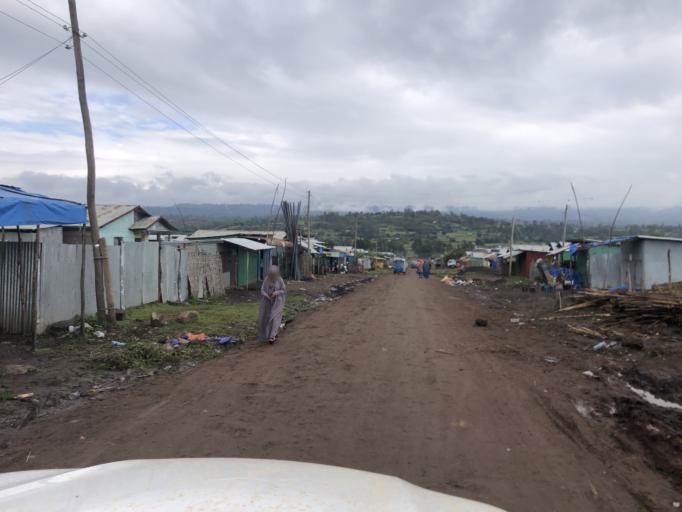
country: ET
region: Southern Nations, Nationalities, and People's Region
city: Butajira
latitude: 7.8386
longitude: 38.1734
